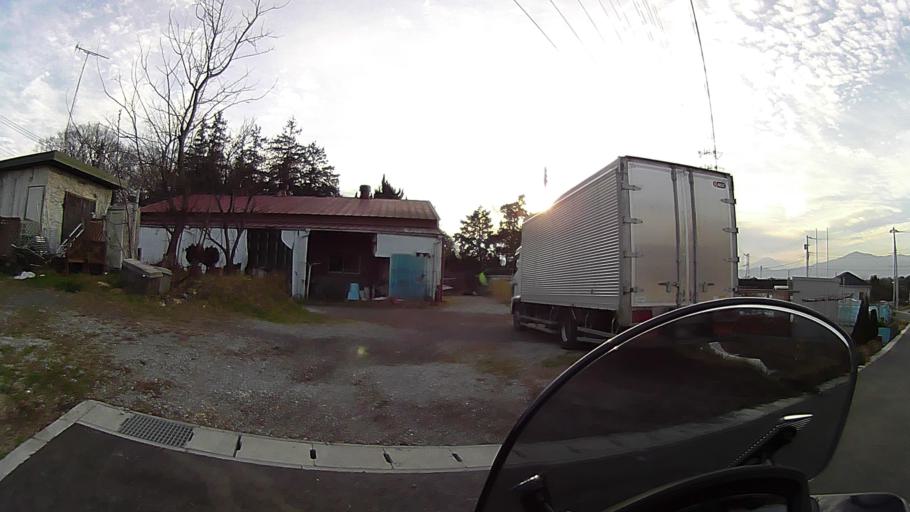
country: JP
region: Kanagawa
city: Atsugi
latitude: 35.4199
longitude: 139.4226
